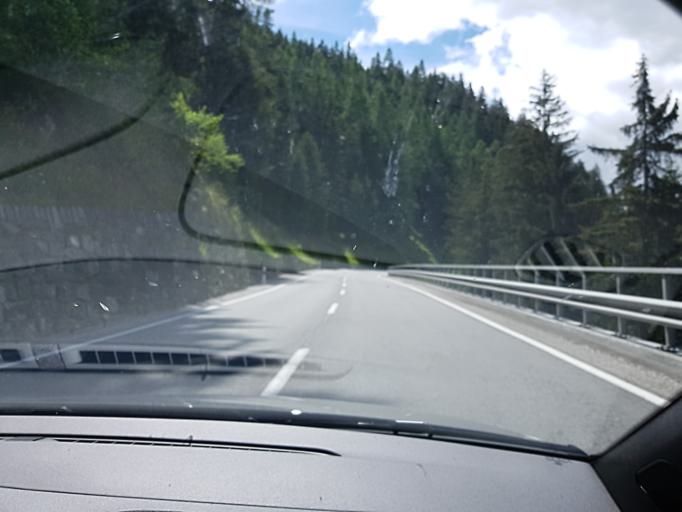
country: CH
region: Grisons
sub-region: Albula District
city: Tiefencastel
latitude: 46.5722
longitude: 9.6236
